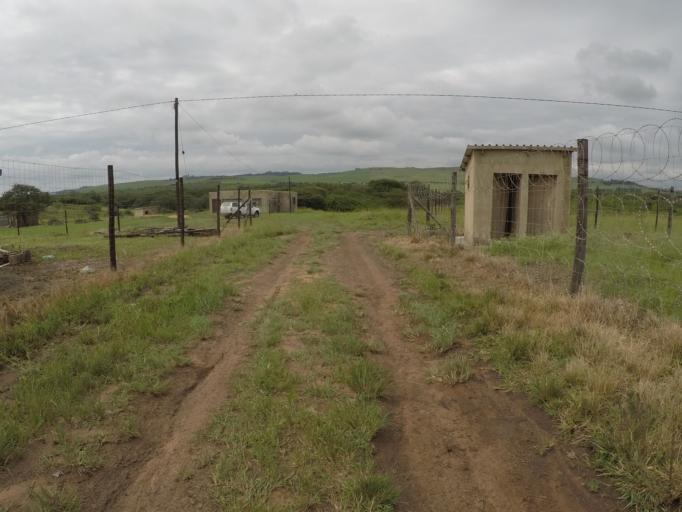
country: ZA
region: KwaZulu-Natal
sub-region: uThungulu District Municipality
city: Empangeni
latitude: -28.7134
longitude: 31.8536
